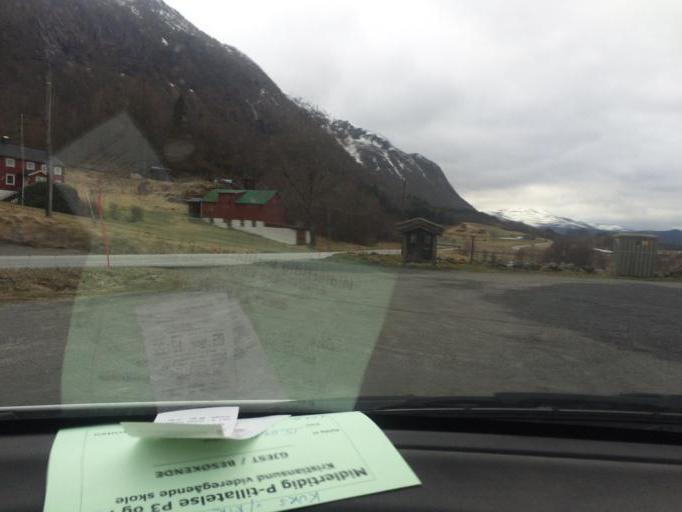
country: NO
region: More og Romsdal
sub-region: Gjemnes
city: Batnfjordsora
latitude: 62.9630
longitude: 7.7784
